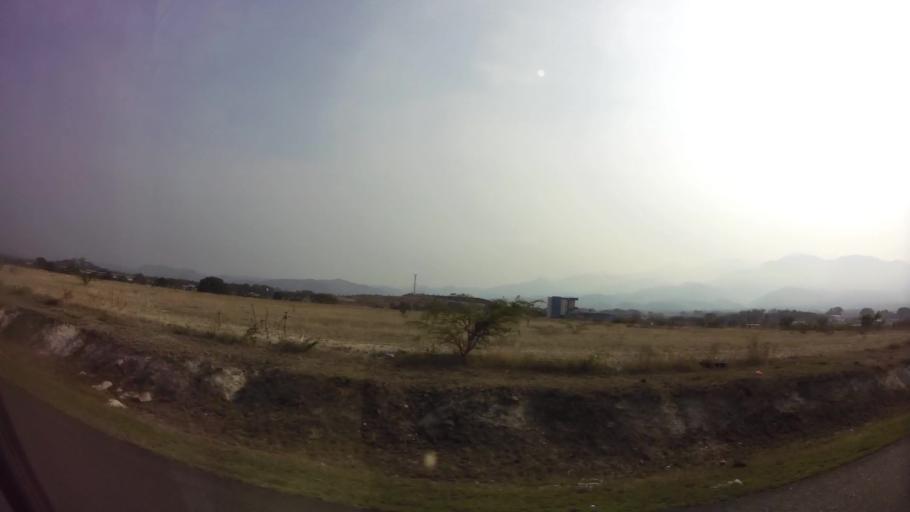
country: HN
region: Comayagua
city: Comayagua
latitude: 14.4267
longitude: -87.6365
